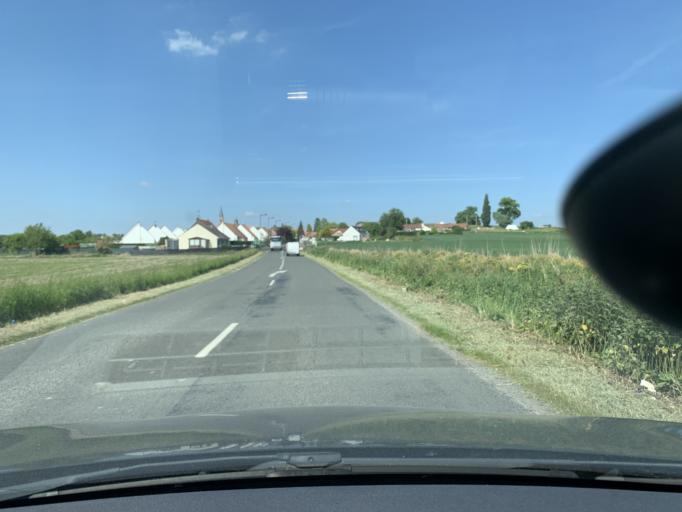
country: FR
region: Nord-Pas-de-Calais
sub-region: Departement du Pas-de-Calais
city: Oisy-le-Verger
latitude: 50.2429
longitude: 3.1158
